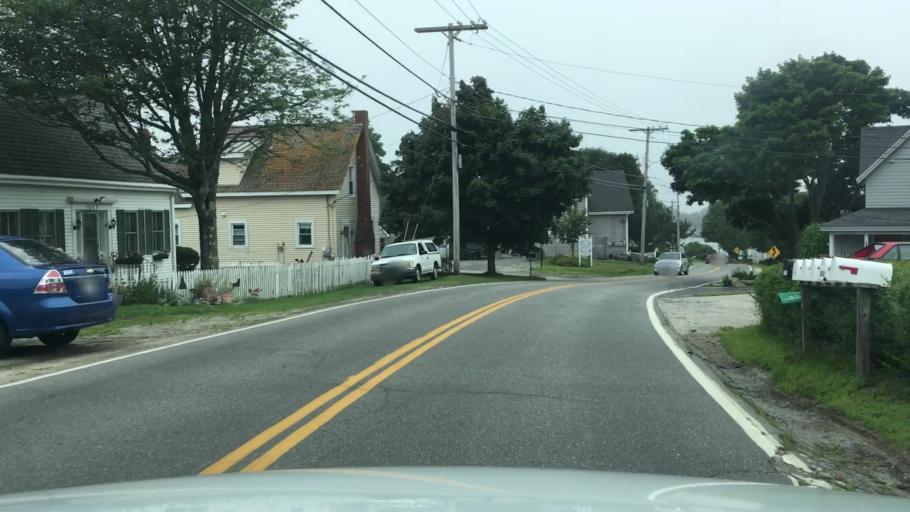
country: US
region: Maine
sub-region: Cumberland County
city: Harpswell Center
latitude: 43.7518
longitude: -69.9847
